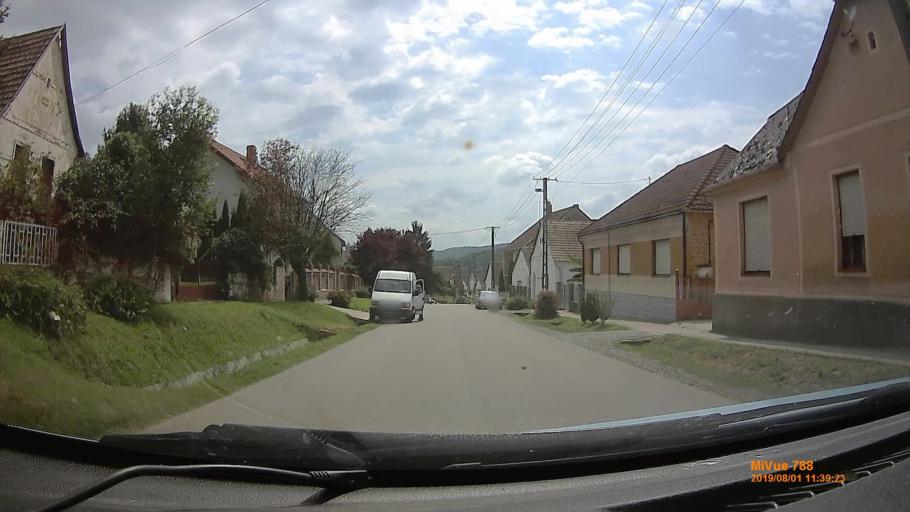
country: HU
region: Baranya
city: Villany
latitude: 45.8946
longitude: 18.3920
